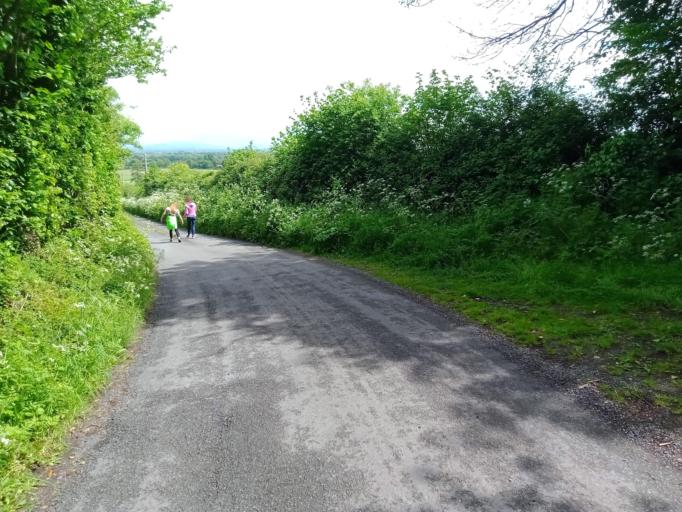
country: IE
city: Ballylinan
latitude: 52.9642
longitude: -7.0717
